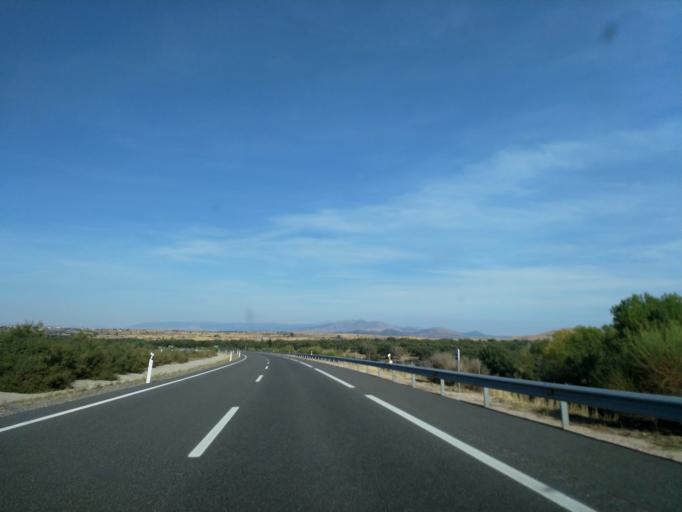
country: ES
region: Castille and Leon
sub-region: Provincia de Segovia
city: Villacastin
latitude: 40.7517
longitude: -4.4576
